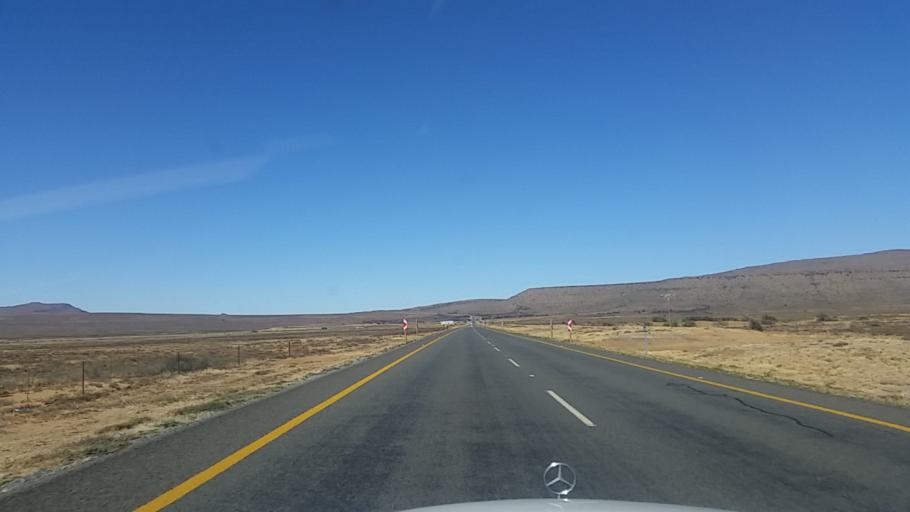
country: ZA
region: Eastern Cape
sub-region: Cacadu District Municipality
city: Graaff-Reinet
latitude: -31.9259
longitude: 24.7492
